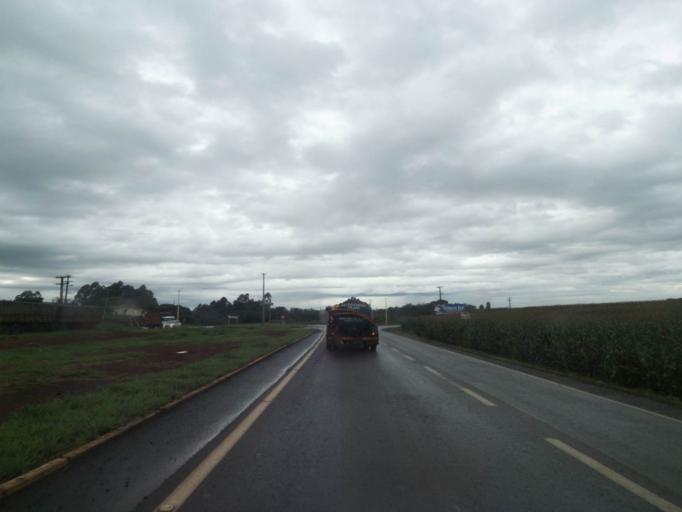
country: BR
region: Parana
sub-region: Toledo
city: Toledo
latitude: -24.6896
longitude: -53.7670
